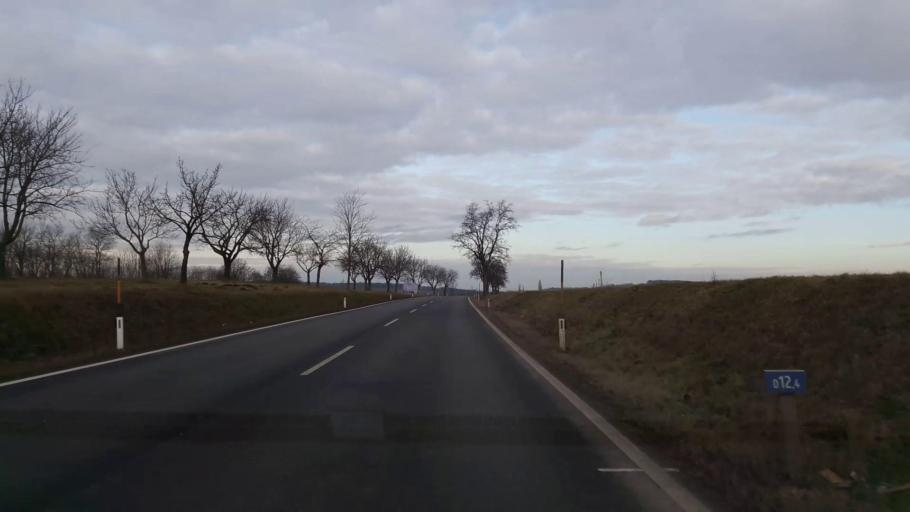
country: AT
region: Lower Austria
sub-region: Politischer Bezirk Mistelbach
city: Mistelbach
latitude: 48.5912
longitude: 16.5499
